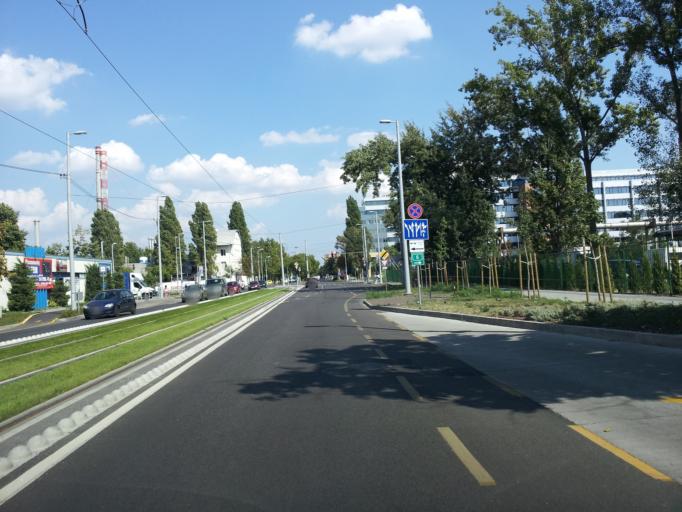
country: HU
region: Budapest
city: Budapest XI. keruelet
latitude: 47.4618
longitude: 19.0465
